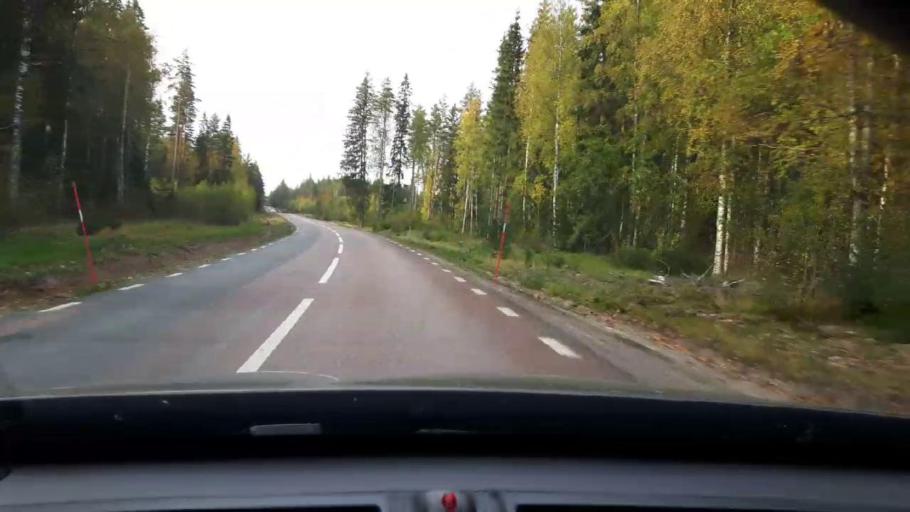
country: SE
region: Dalarna
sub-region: Gagnefs Kommun
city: Mockfjard
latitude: 60.3207
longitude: 14.9378
